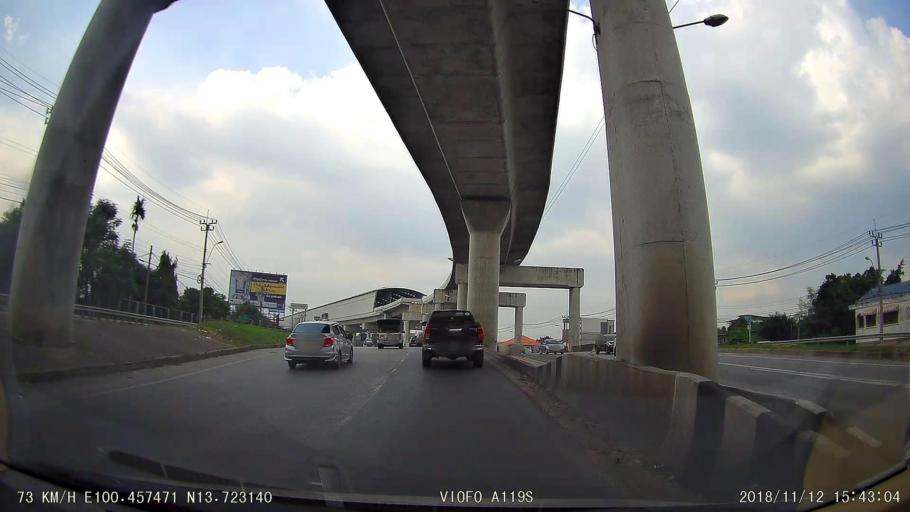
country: TH
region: Bangkok
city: Bangkok Yai
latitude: 13.7231
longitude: 100.4575
